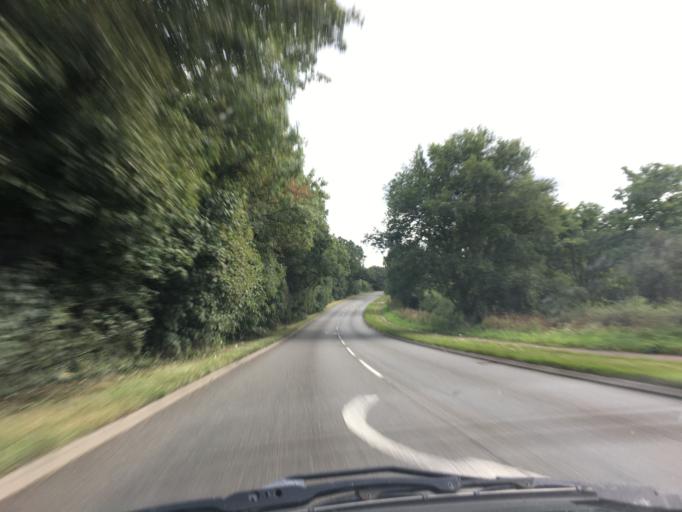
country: GB
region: England
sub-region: Leicestershire
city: Lutterworth
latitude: 52.4465
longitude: -1.1960
